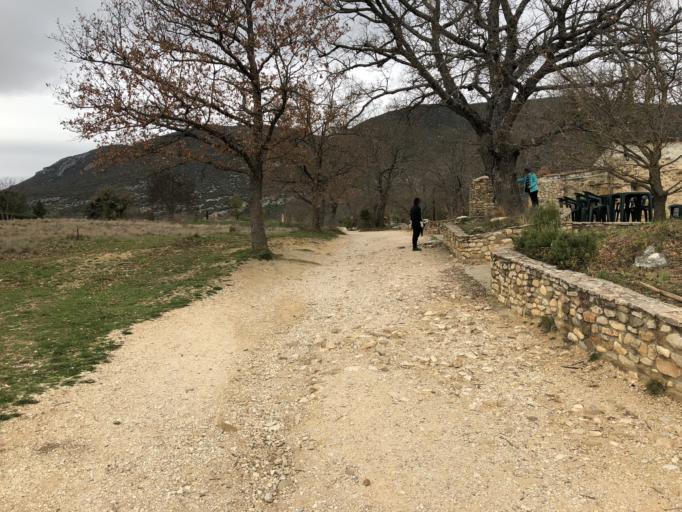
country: FR
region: Provence-Alpes-Cote d'Azur
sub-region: Departement du Vaucluse
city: Saignon
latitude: 43.9164
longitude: 5.4970
